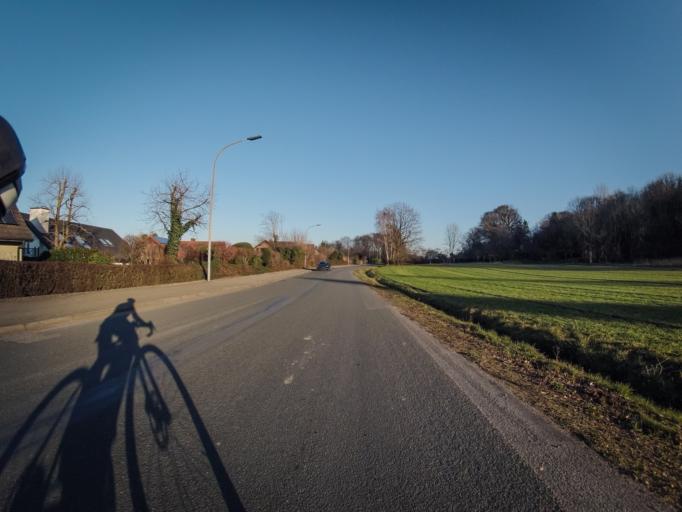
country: DE
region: Lower Saxony
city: Wallenhorst
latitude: 52.3267
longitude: 8.0206
